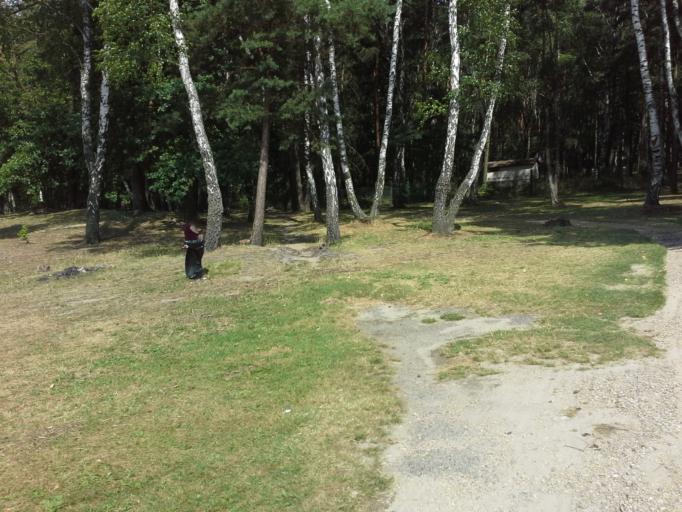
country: PL
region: Lesser Poland Voivodeship
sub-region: Powiat chrzanowski
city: Trzebinia
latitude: 50.1386
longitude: 19.4510
